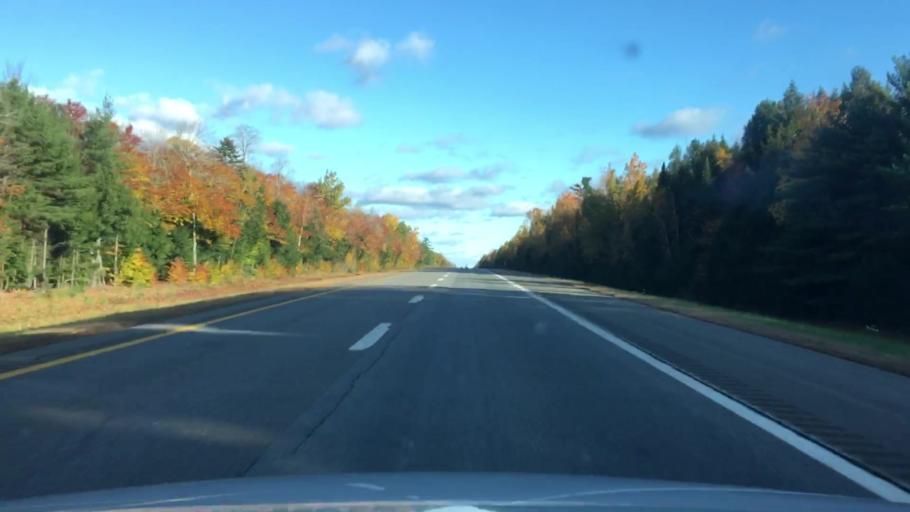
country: US
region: Maine
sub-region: Penobscot County
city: Greenbush
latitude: 45.0676
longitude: -68.6897
